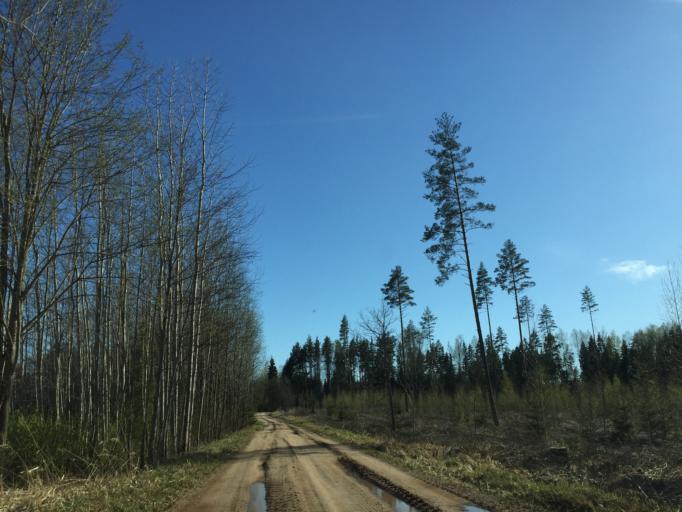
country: EE
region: Valgamaa
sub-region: Valga linn
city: Valga
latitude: 57.7787
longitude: 26.2325
